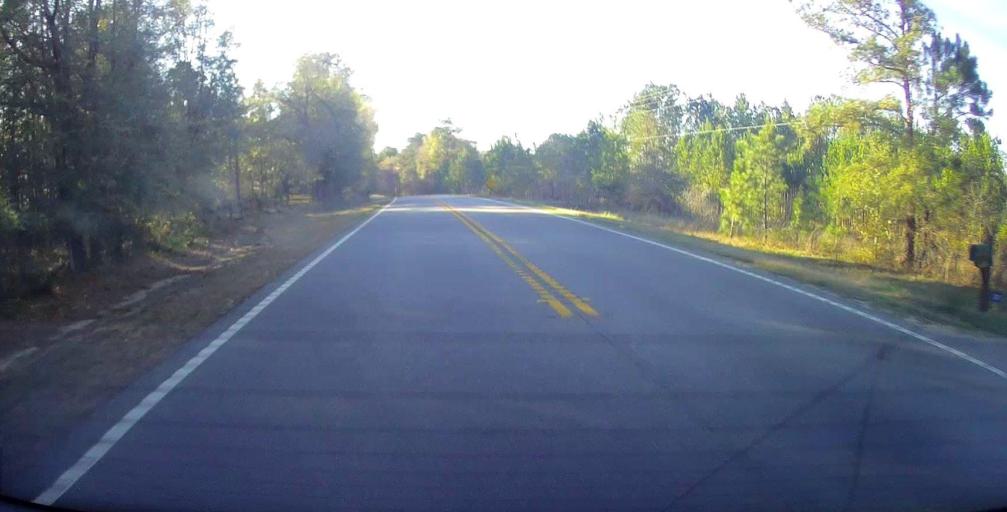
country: US
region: Georgia
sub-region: Pulaski County
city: Hawkinsville
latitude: 32.2687
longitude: -83.4339
